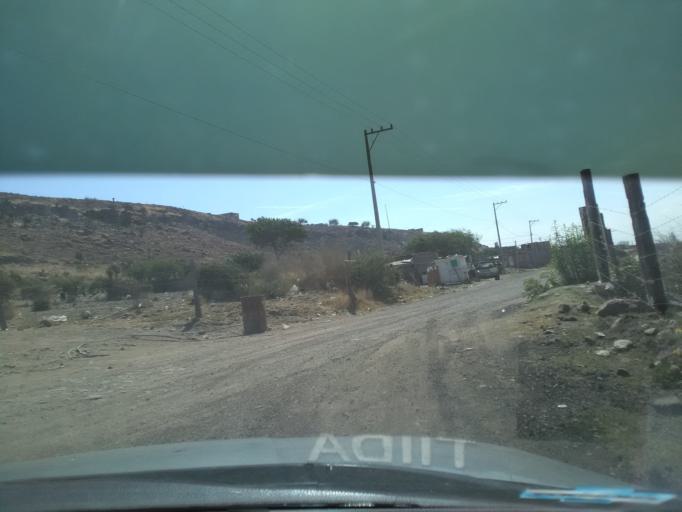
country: MX
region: Durango
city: Victoria de Durango
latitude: 24.0334
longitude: -104.7156
